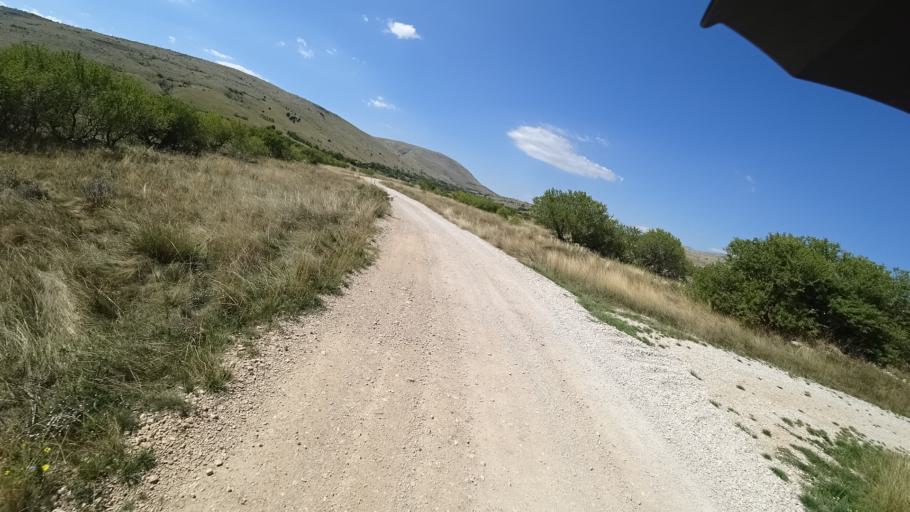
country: HR
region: Splitsko-Dalmatinska
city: Hrvace
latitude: 43.8497
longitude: 16.6458
